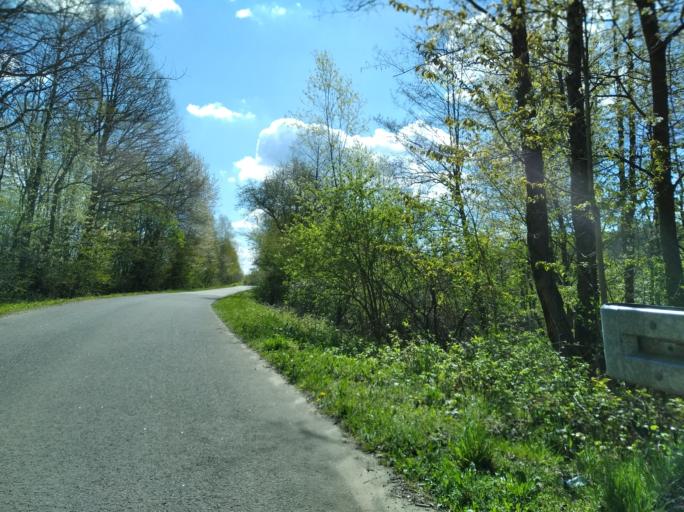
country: PL
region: Subcarpathian Voivodeship
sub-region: Powiat brzozowski
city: Golcowa
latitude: 49.7906
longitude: 22.0427
